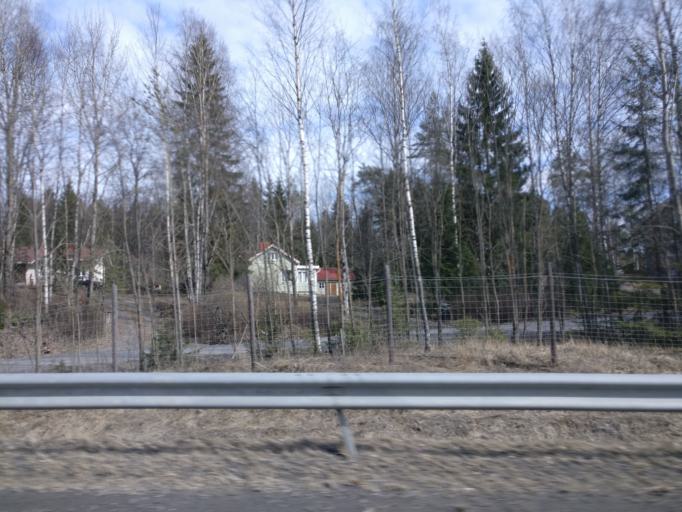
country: FI
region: Pirkanmaa
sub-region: Tampere
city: Tampere
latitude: 61.4243
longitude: 23.7552
